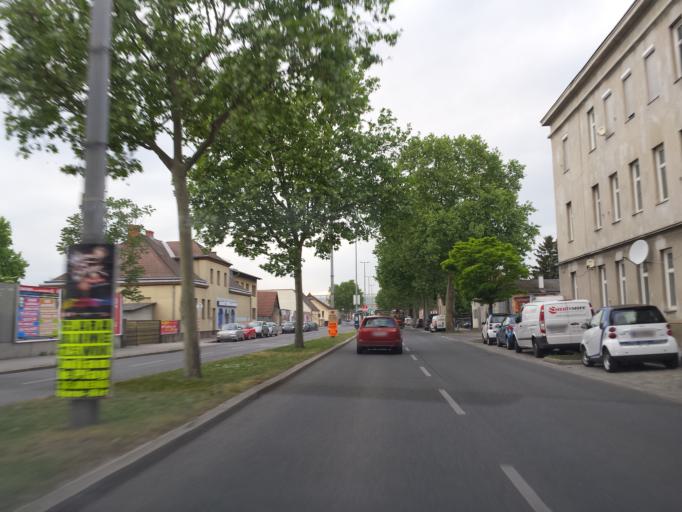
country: AT
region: Lower Austria
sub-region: Politischer Bezirk Wien-Umgebung
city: Gerasdorf bei Wien
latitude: 48.2211
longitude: 16.4778
